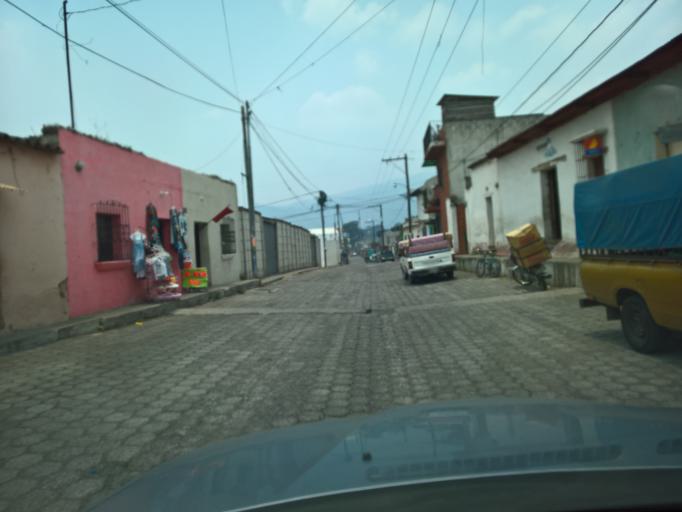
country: GT
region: Sacatepequez
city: Ciudad Vieja
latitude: 14.5263
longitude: -90.7510
